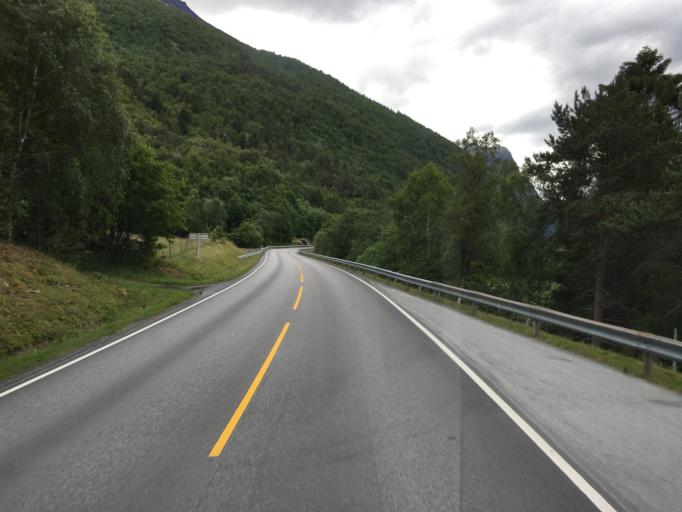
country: NO
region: More og Romsdal
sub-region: Sunndal
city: Sunndalsora
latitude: 62.6440
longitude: 8.7212
